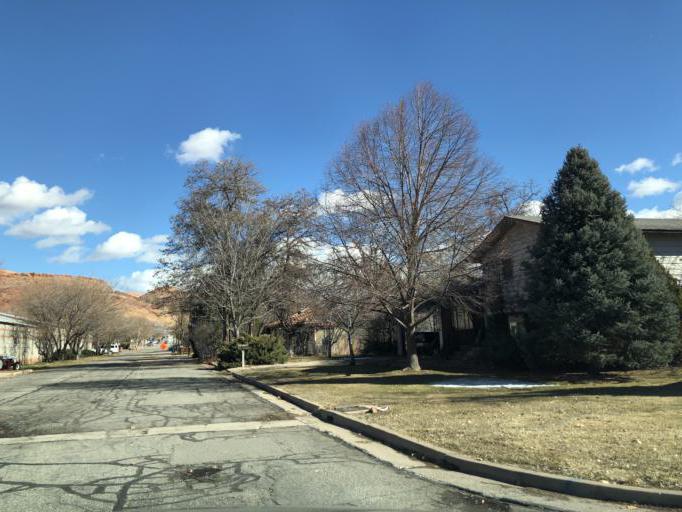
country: US
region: Utah
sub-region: Grand County
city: Moab
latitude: 38.5764
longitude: -109.5548
